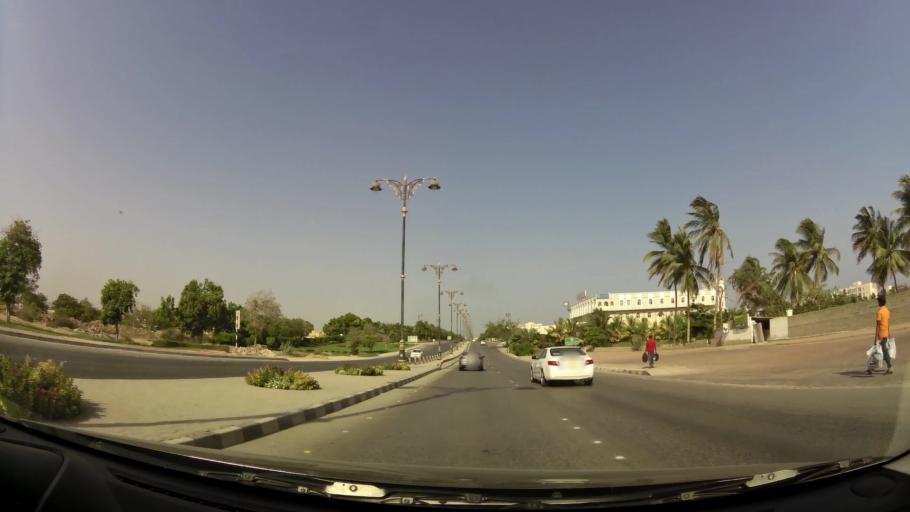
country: OM
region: Zufar
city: Salalah
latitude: 17.0046
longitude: 54.0437
